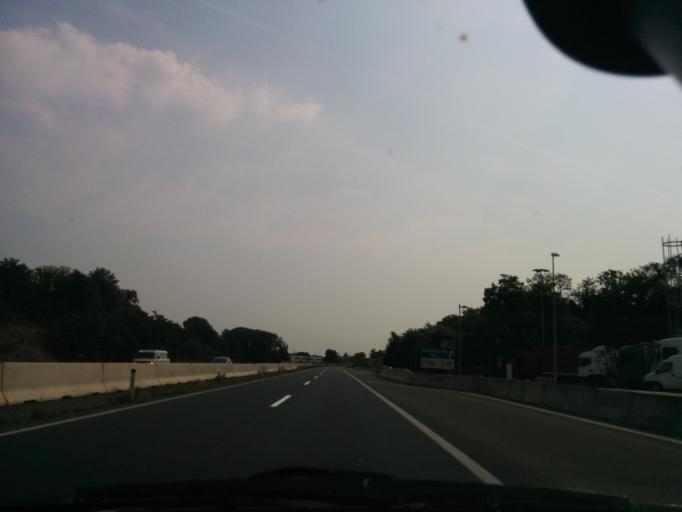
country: AT
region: Lower Austria
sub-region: Politischer Bezirk Korneuburg
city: Stockerau
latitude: 48.3811
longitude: 16.2041
